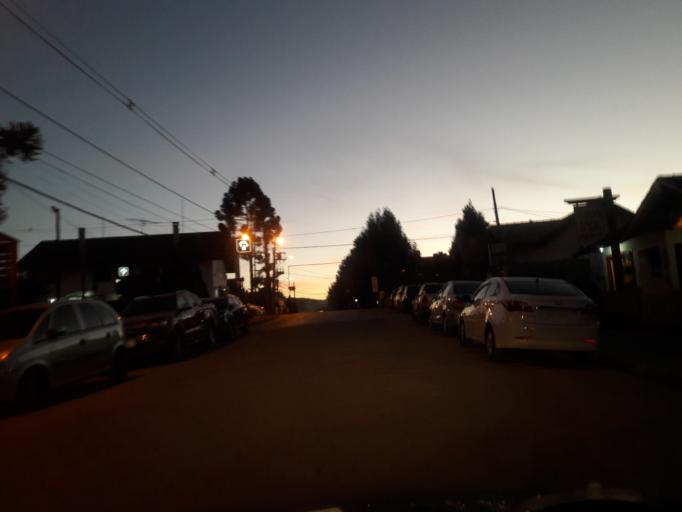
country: BR
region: Minas Gerais
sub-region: Camanducaia
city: Camanducaia
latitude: -22.8626
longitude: -46.0349
